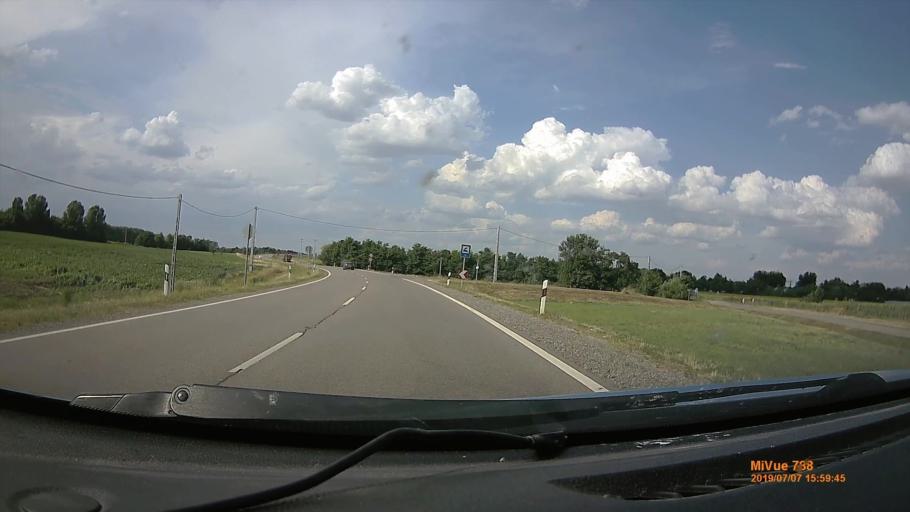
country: HU
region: Heves
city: Boldog
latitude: 47.5902
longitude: 19.7491
